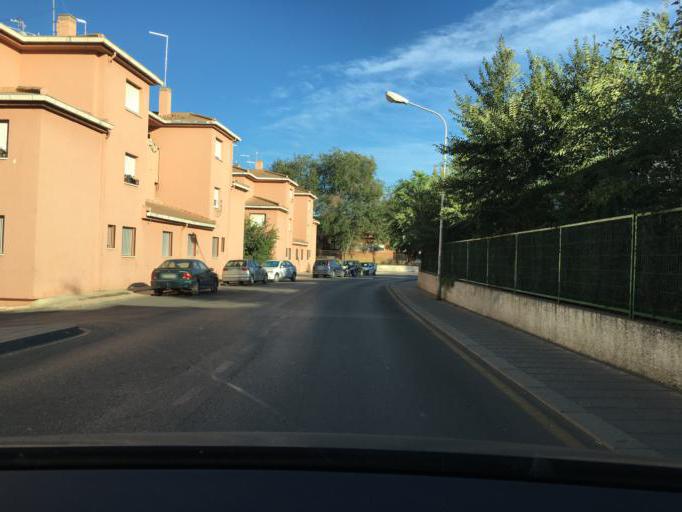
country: ES
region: Andalusia
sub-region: Provincia de Granada
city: Guadix
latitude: 37.2968
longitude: -3.1326
